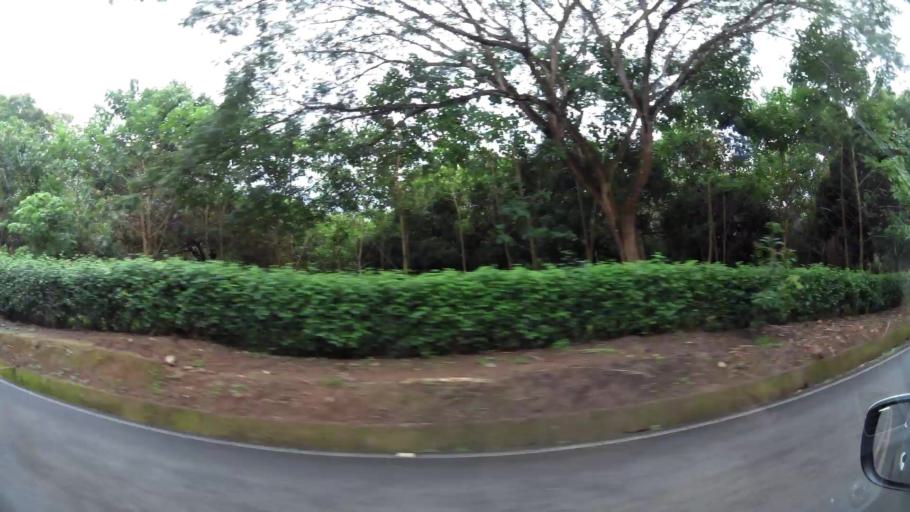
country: CR
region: Puntarenas
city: Esparza
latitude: 9.9854
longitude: -84.6273
